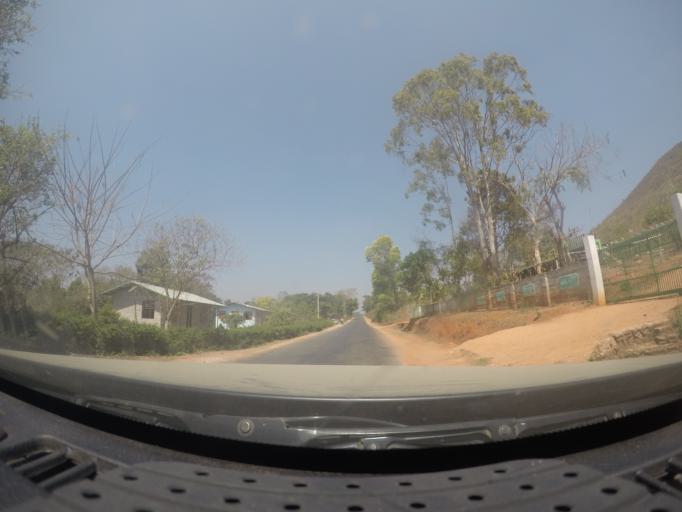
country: MM
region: Shan
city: Taunggyi
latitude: 20.9644
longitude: 96.5421
